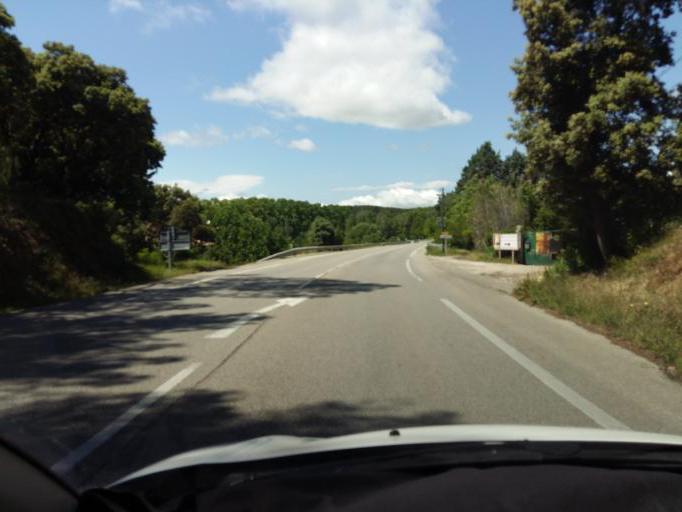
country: FR
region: Provence-Alpes-Cote d'Azur
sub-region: Departement des Bouches-du-Rhone
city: Lambesc
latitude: 43.6575
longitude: 5.2567
